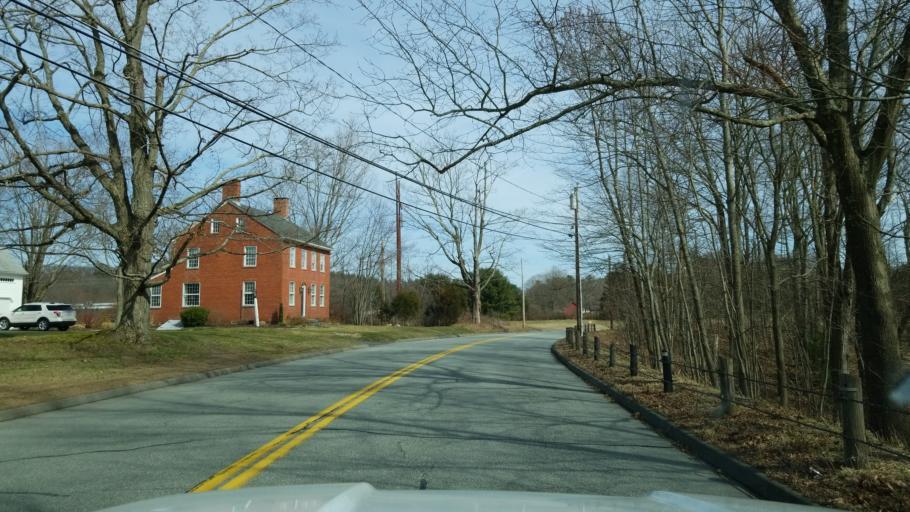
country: US
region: Connecticut
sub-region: Hartford County
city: Glastonbury Center
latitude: 41.7006
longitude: -72.5498
